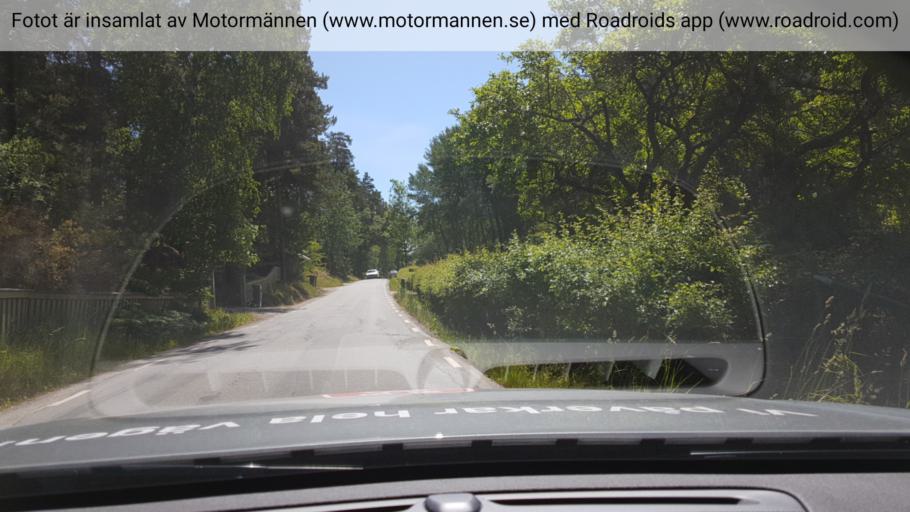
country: SE
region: Stockholm
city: Dalaro
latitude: 59.1489
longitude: 18.4331
